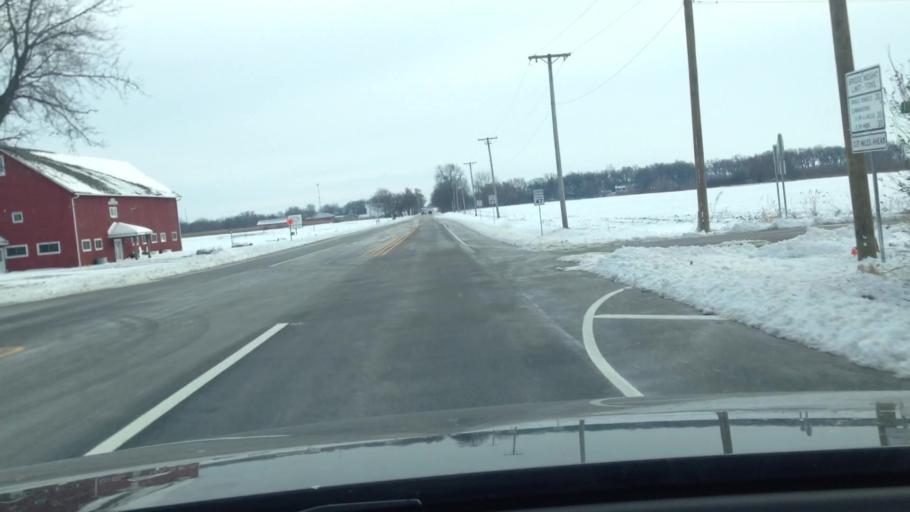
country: US
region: Illinois
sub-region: McHenry County
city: Hebron
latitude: 42.4145
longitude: -88.4382
